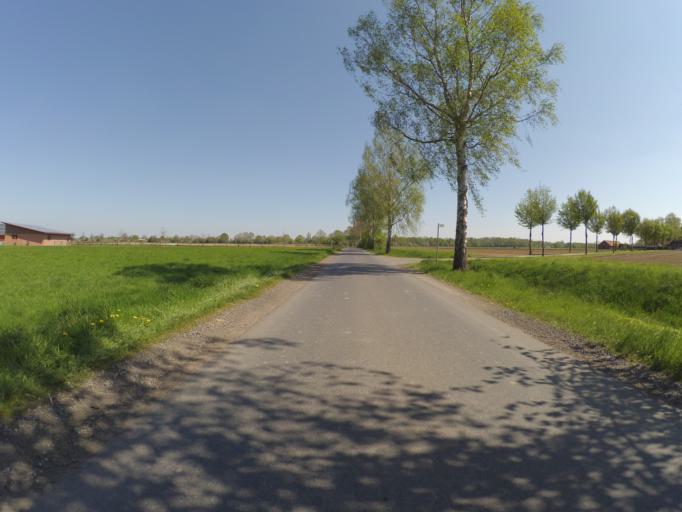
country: DE
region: North Rhine-Westphalia
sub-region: Regierungsbezirk Munster
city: Ascheberg
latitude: 51.7871
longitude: 7.5910
